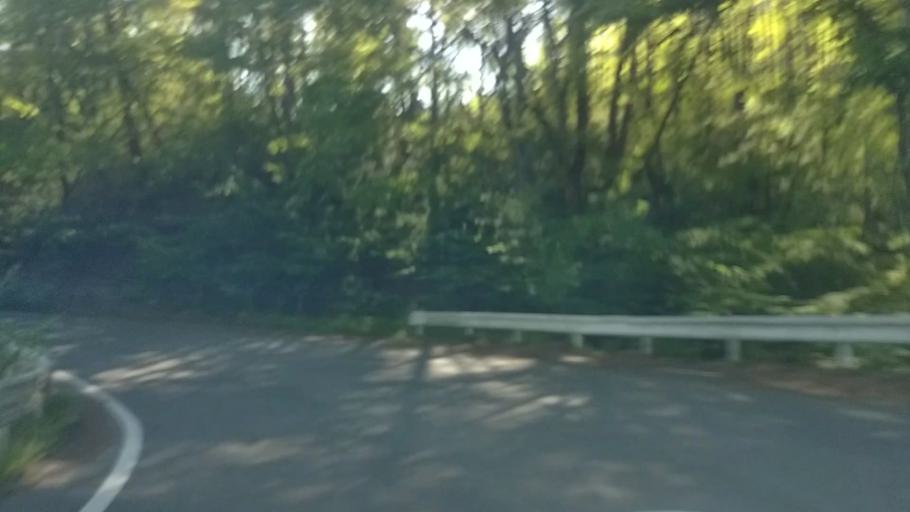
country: JP
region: Yamanashi
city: Nirasaki
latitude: 35.8929
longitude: 138.3992
